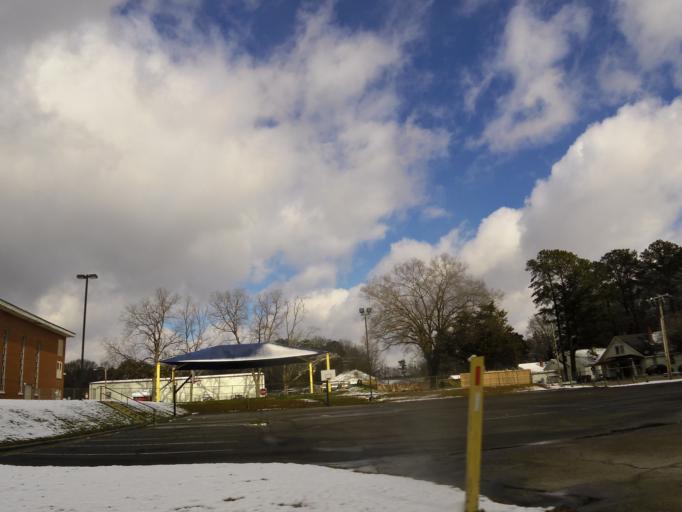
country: US
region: North Carolina
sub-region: Wilson County
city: Wilson
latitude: 35.7215
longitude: -77.9281
